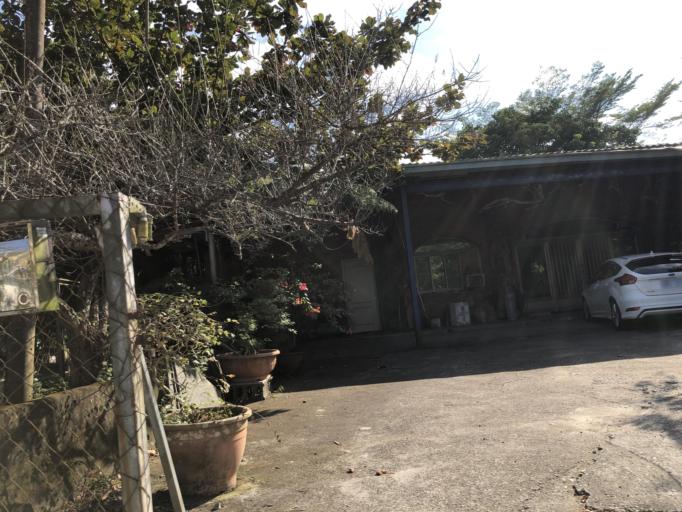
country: TW
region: Taiwan
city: Yujing
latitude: 23.0083
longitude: 120.3982
